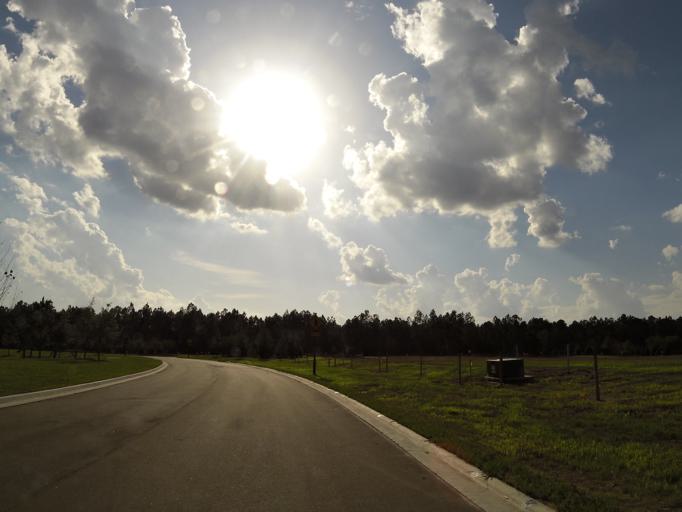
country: US
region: Florida
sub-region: Clay County
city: Green Cove Springs
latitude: 30.0304
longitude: -81.6326
